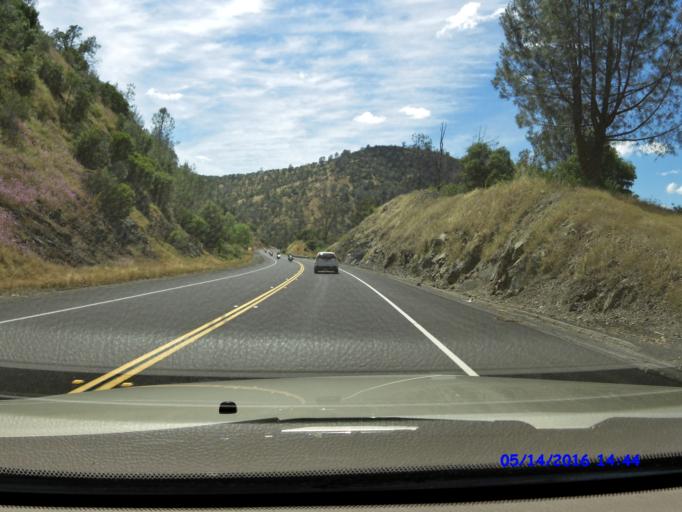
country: US
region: California
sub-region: Tuolumne County
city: Jamestown
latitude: 37.8403
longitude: -120.3707
